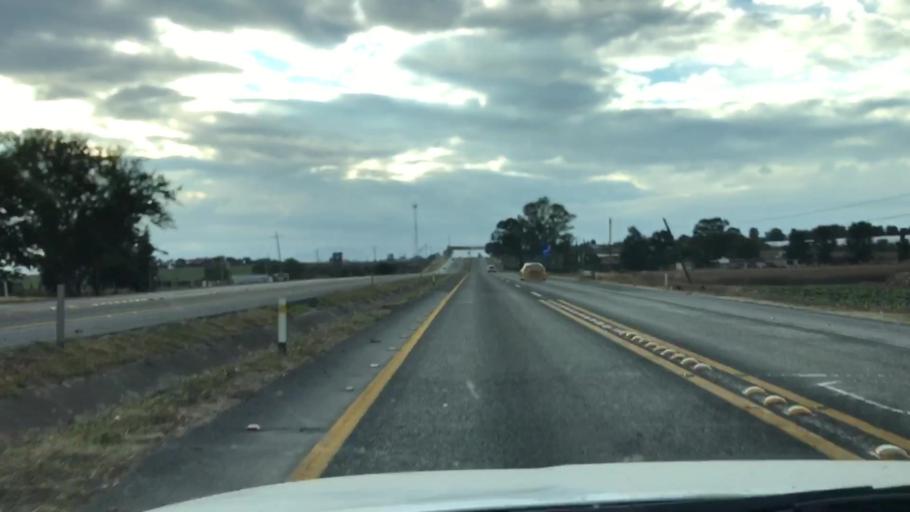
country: MX
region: Guanajuato
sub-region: Penjamo
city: Mezquite de Luna
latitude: 20.3801
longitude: -101.8290
